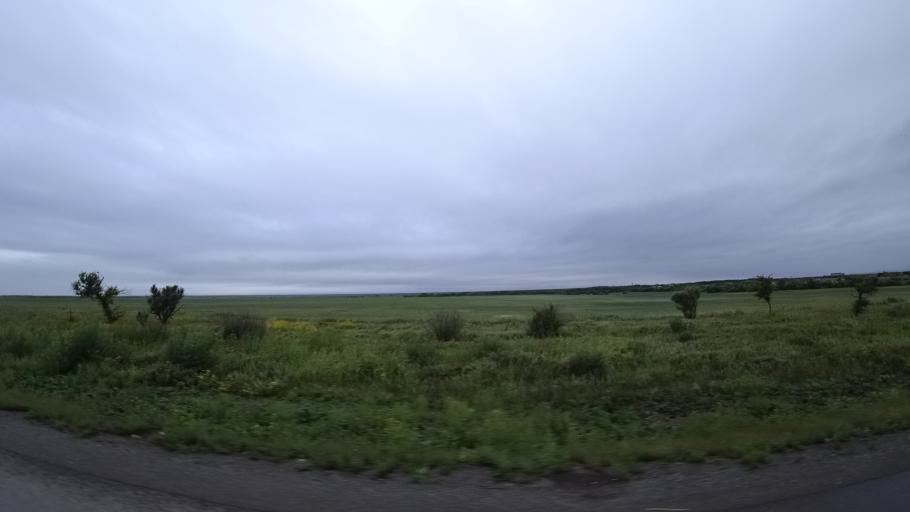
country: RU
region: Primorskiy
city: Chernigovka
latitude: 44.3064
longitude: 132.5392
